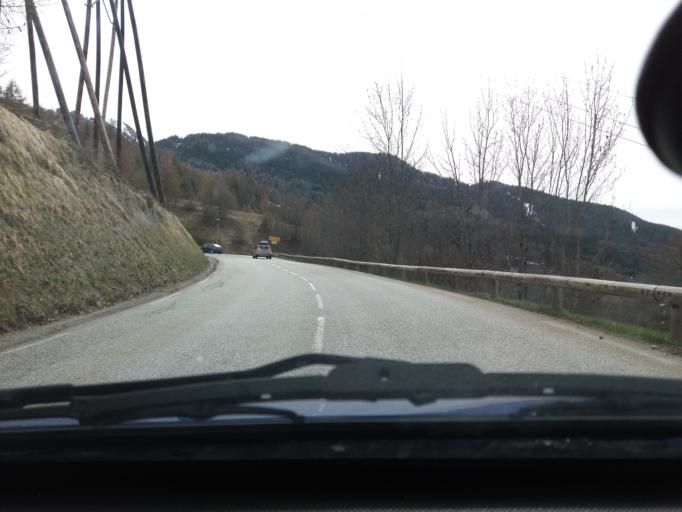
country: FR
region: Rhone-Alpes
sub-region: Departement de la Savoie
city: Macot-la-Plagne
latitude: 45.5401
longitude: 6.6700
